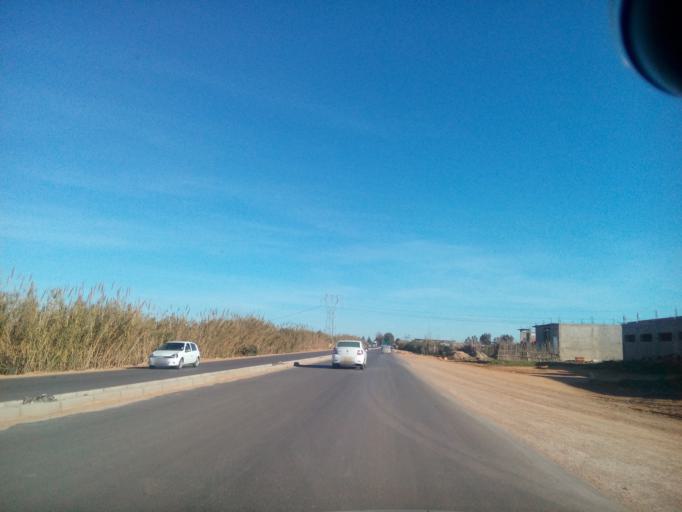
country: DZ
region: Mostaganem
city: Mostaganem
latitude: 35.9057
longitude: 0.1850
